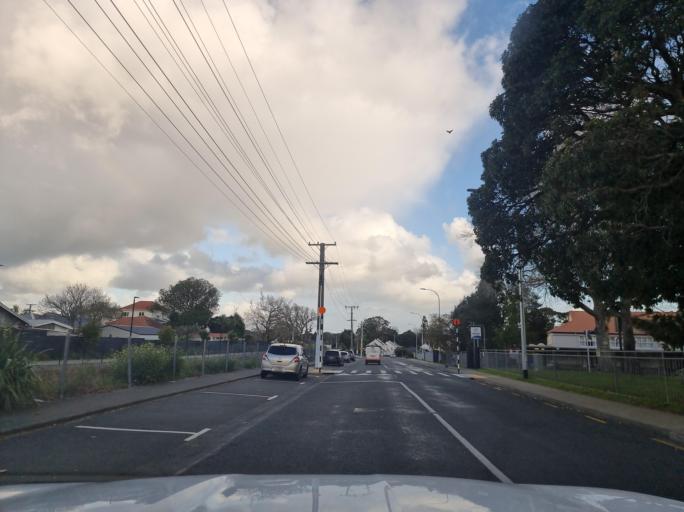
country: NZ
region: Northland
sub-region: Whangarei
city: Whangarei
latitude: -35.7135
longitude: 174.3199
